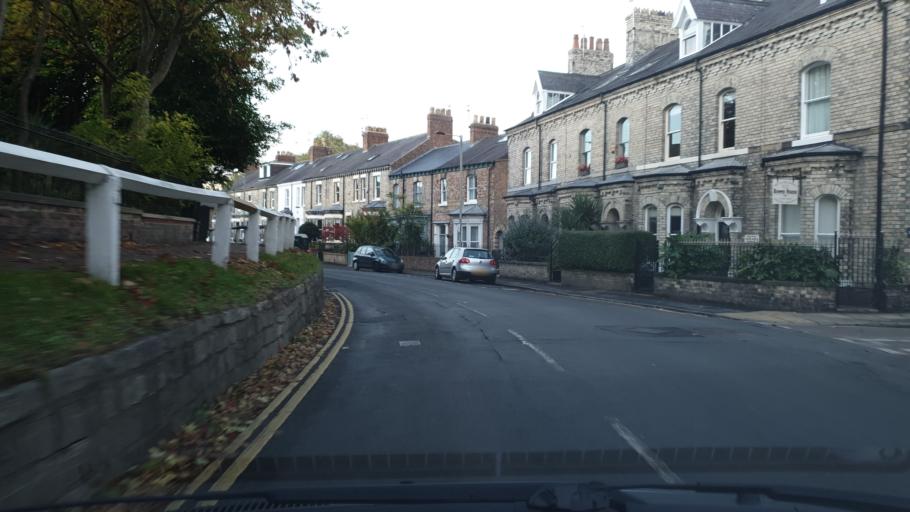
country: GB
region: England
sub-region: City of York
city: York
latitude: 53.9677
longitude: -1.0725
